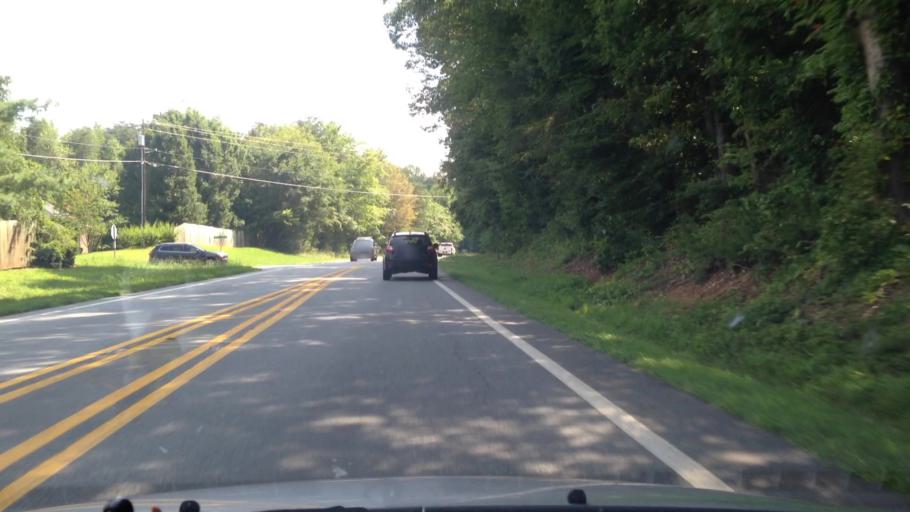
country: US
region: North Carolina
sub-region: Guilford County
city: Oak Ridge
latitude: 36.1853
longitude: -79.9864
